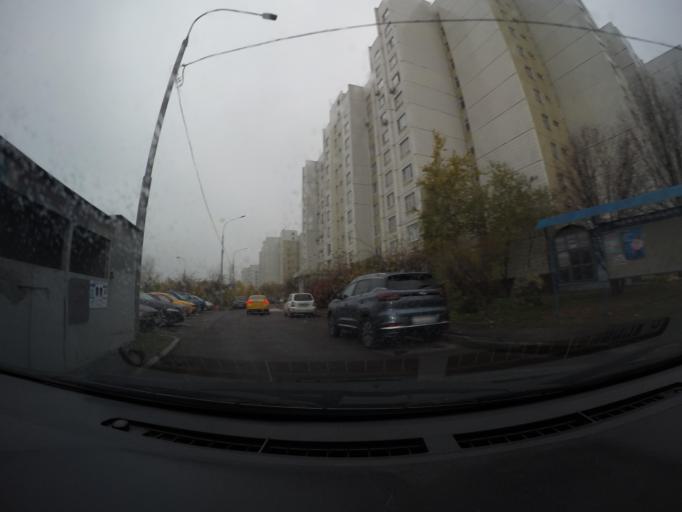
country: RU
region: Moskovskaya
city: Kommunarka
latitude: 55.5474
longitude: 37.5226
